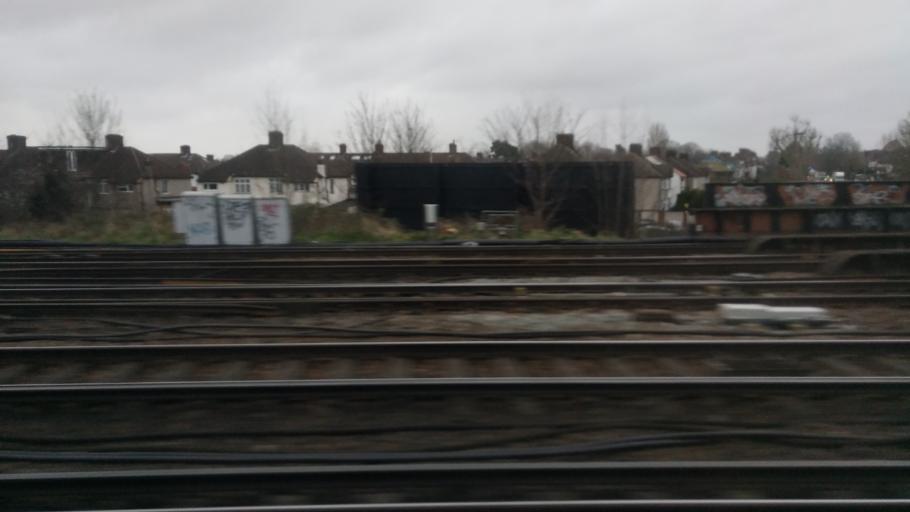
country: GB
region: England
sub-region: Greater London
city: Blackheath
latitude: 51.4456
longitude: 0.0054
